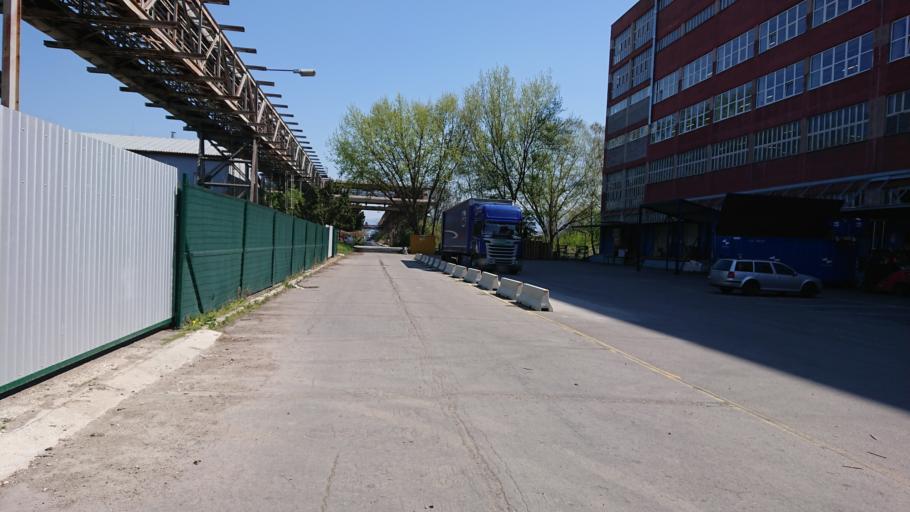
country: SK
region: Nitriansky
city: Partizanske
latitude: 48.6303
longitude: 18.3711
